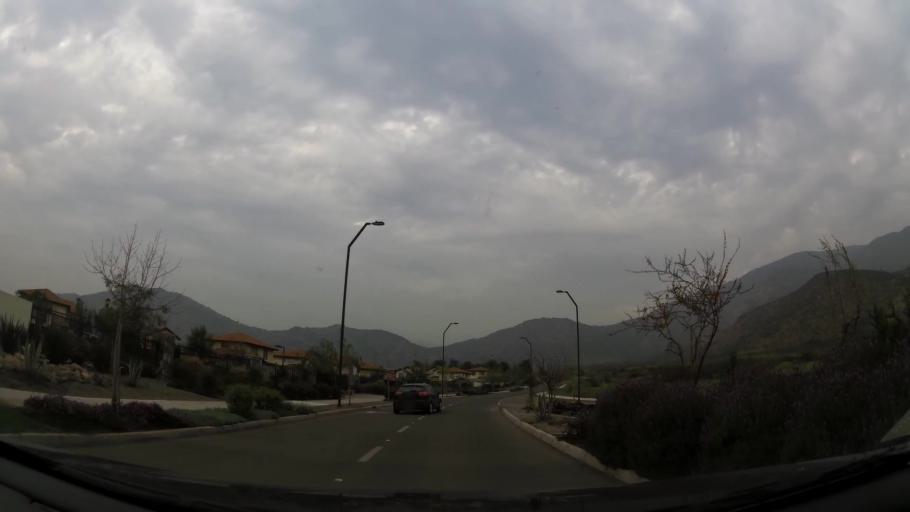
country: CL
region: Santiago Metropolitan
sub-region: Provincia de Chacabuco
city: Chicureo Abajo
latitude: -33.2017
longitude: -70.6487
